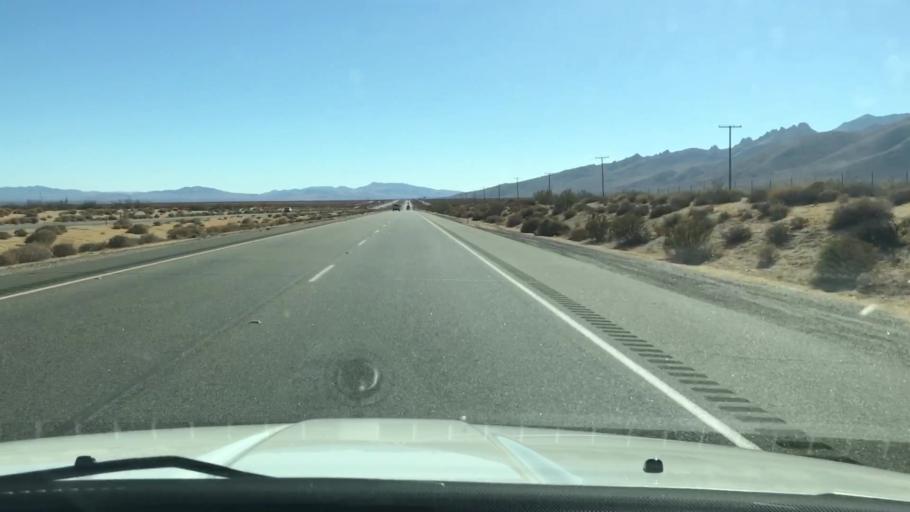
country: US
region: California
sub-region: Kern County
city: Inyokern
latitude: 35.7660
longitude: -117.8713
